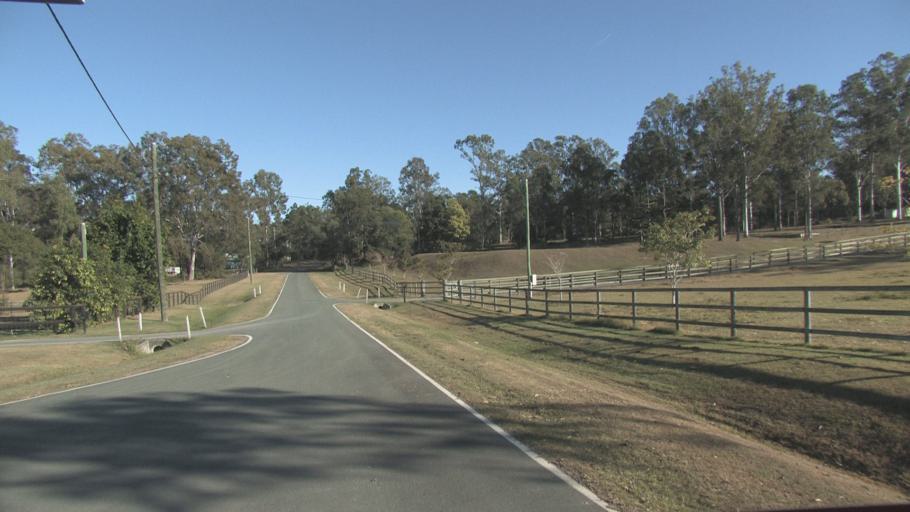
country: AU
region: Queensland
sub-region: Logan
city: North Maclean
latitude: -27.7915
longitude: 152.9629
